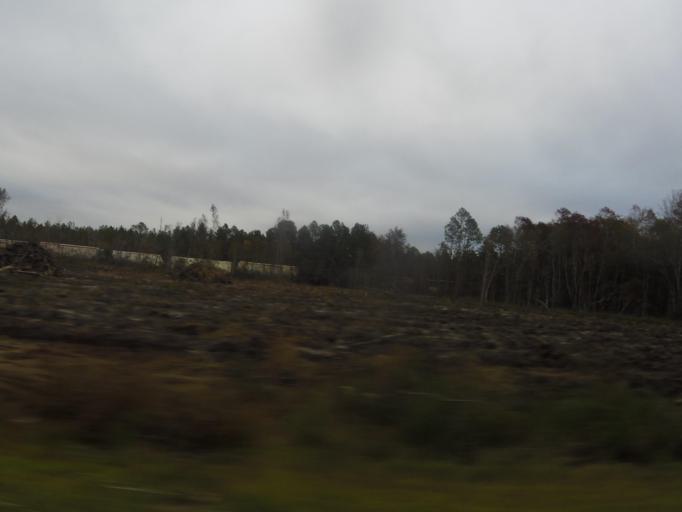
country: US
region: Georgia
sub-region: Charlton County
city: Folkston
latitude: 30.8711
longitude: -82.0440
